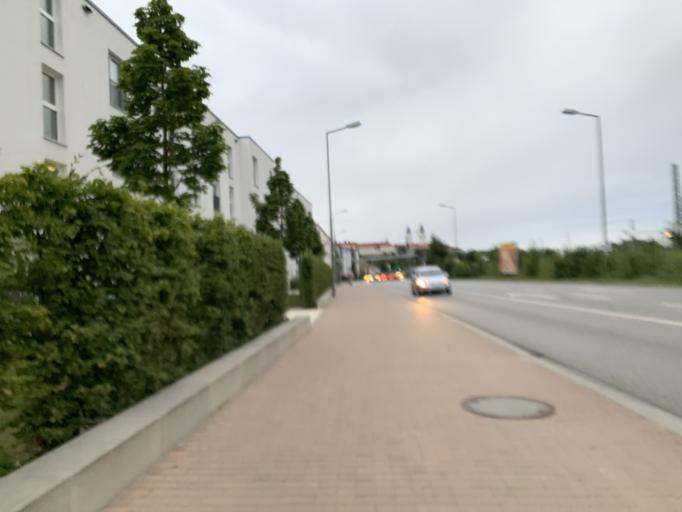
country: DE
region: Bavaria
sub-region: Upper Bavaria
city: Freising
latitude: 48.3924
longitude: 11.7402
